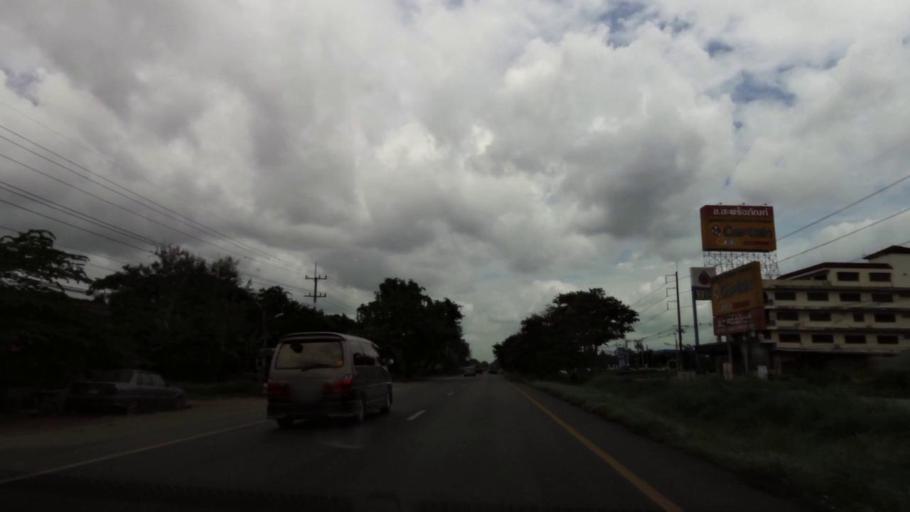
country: TH
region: Rayong
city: Klaeng
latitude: 12.7822
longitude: 101.6921
